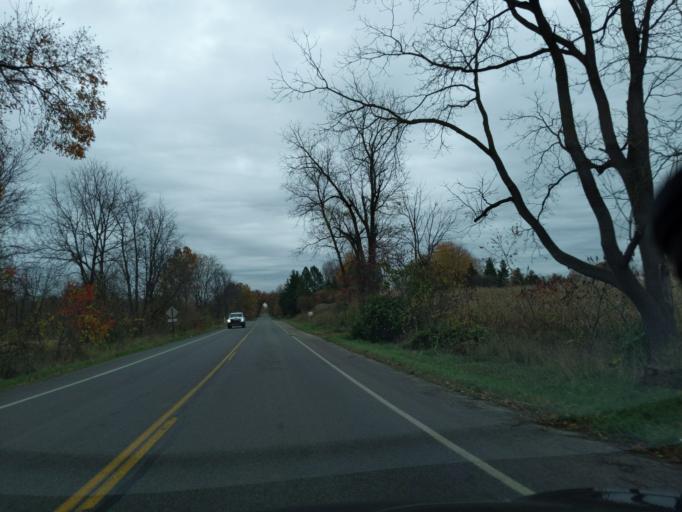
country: US
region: Michigan
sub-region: Jackson County
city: Spring Arbor
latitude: 42.2767
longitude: -84.5505
